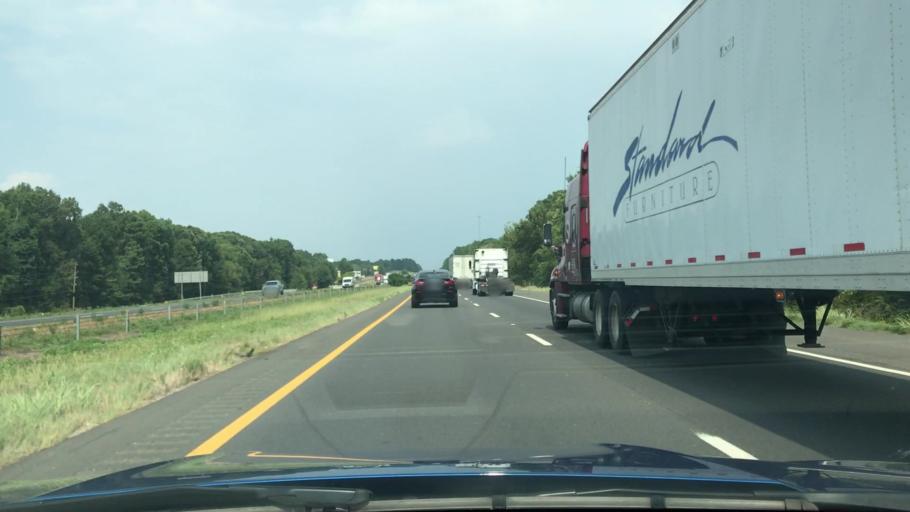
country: US
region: Texas
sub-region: Harrison County
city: Hallsville
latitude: 32.4618
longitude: -94.6549
